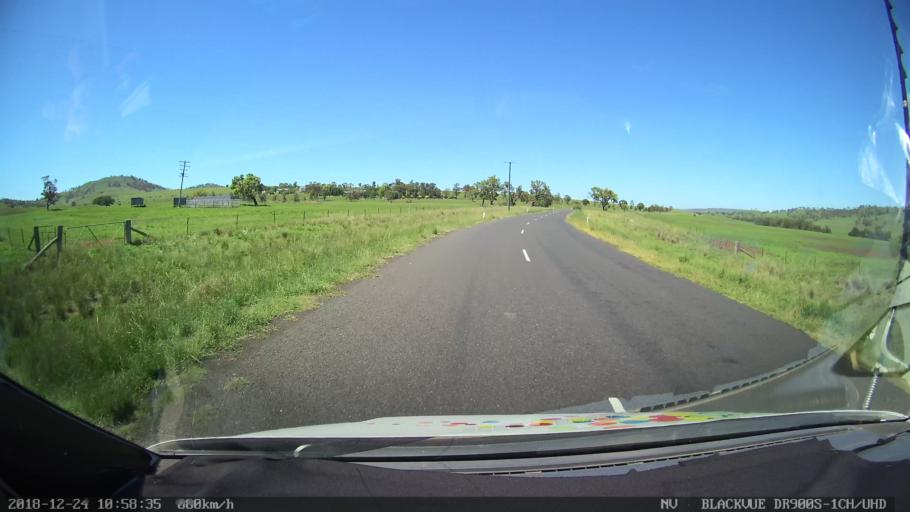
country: AU
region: New South Wales
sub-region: Upper Hunter Shire
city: Merriwa
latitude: -32.0493
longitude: 150.4057
